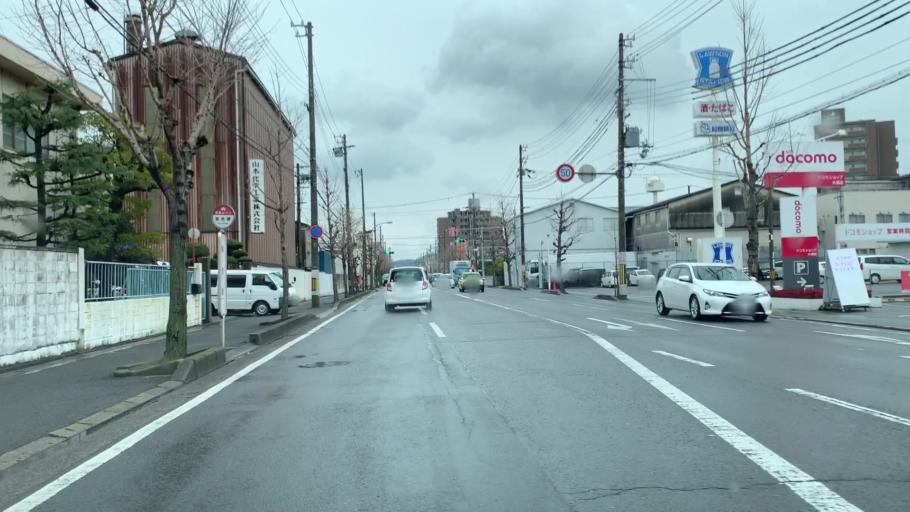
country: JP
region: Wakayama
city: Wakayama-shi
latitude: 34.2240
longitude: 135.1596
